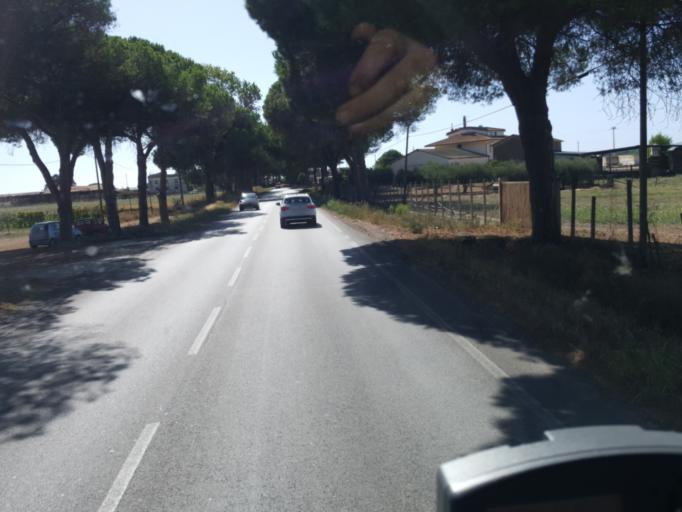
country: IT
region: Latium
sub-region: Citta metropolitana di Roma Capitale
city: Nettuno
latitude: 41.5113
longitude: 12.6959
